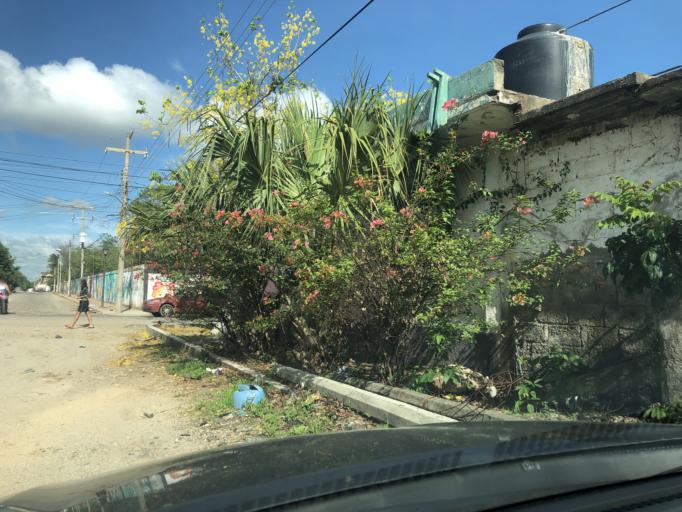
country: MX
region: Oaxaca
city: San Jeronimo Ixtepec
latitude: 16.5605
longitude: -95.1050
